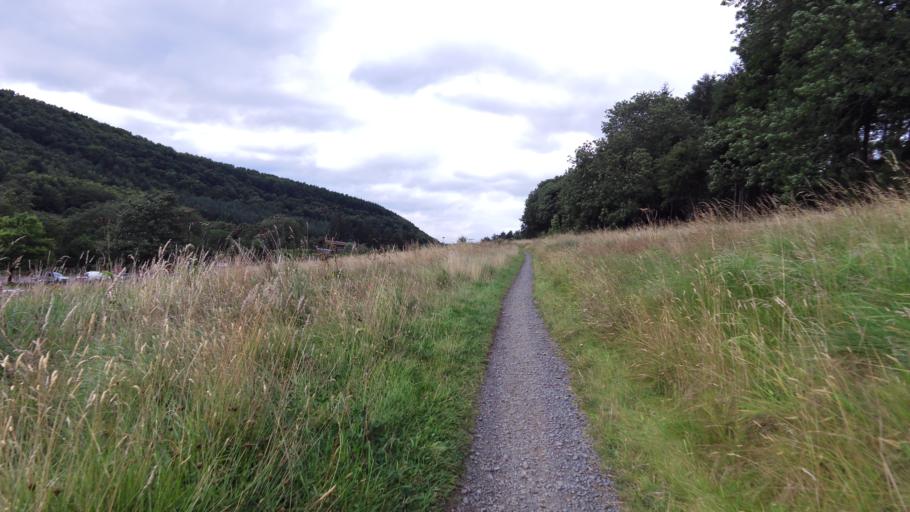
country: GB
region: England
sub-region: North Yorkshire
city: Thornton Dale
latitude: 54.2767
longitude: -0.6864
